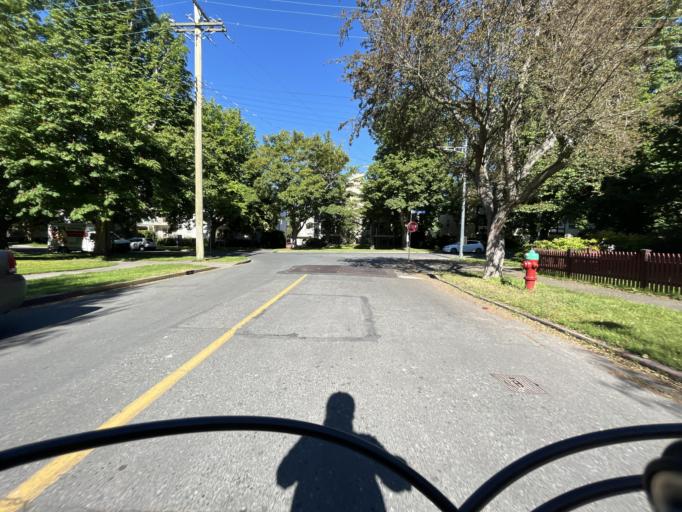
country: CA
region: British Columbia
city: Victoria
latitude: 48.4199
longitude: -123.3575
